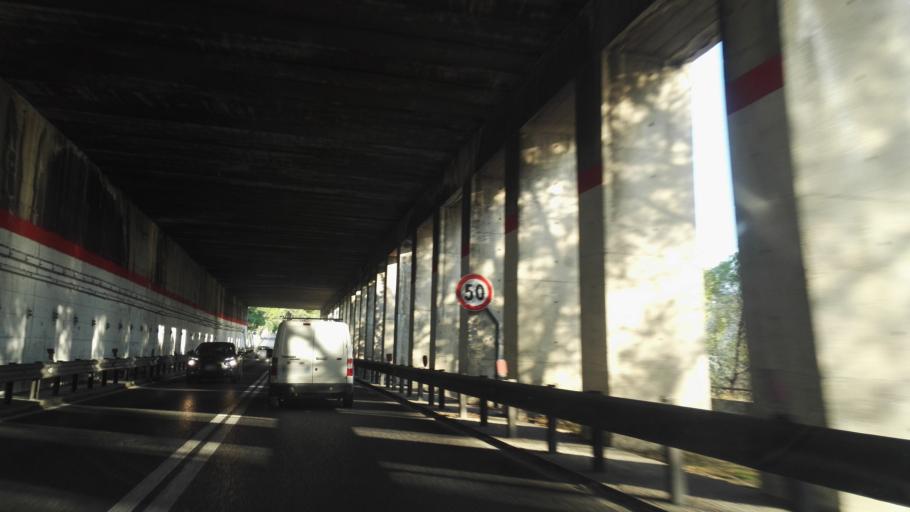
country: IT
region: Calabria
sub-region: Provincia di Catanzaro
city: Squillace Lido
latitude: 38.7655
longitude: 16.5652
